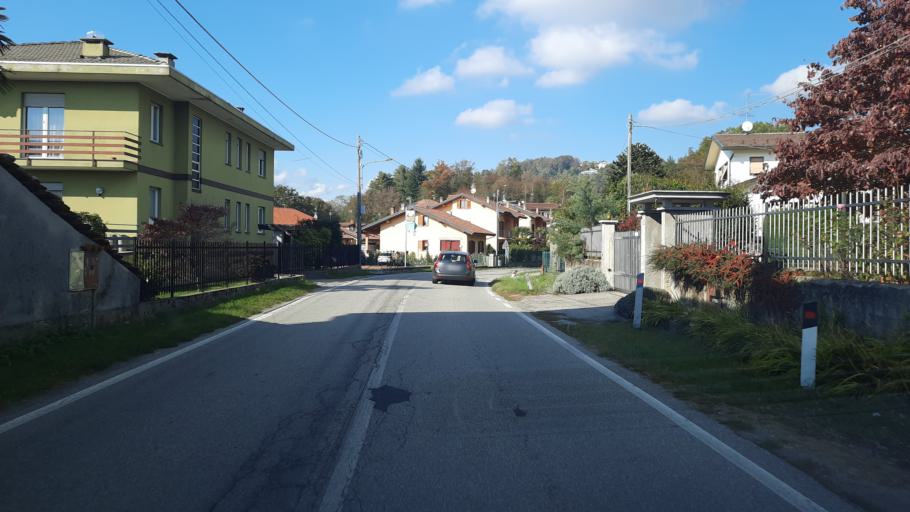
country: IT
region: Piedmont
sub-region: Provincia di Novara
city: Bolzano Novarese
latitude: 45.7647
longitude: 8.4445
